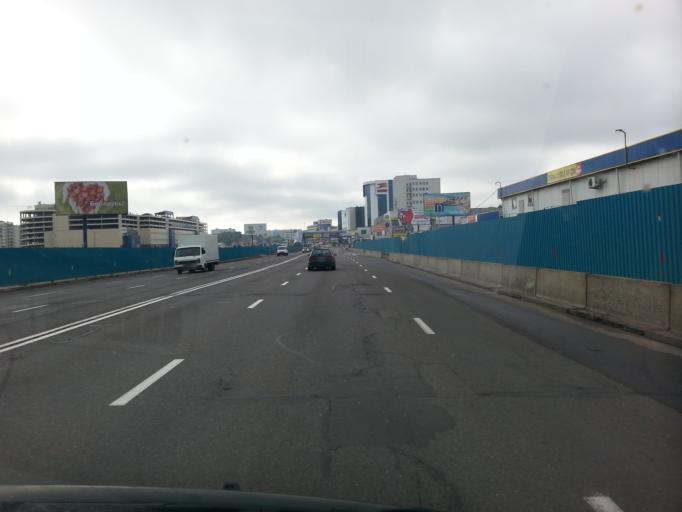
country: BY
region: Minsk
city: Zhdanovichy
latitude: 53.9353
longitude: 27.4525
